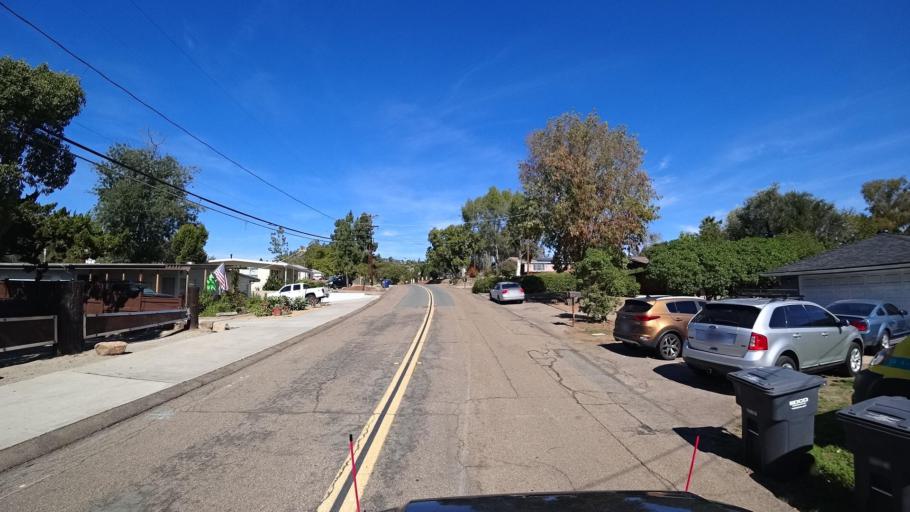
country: US
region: California
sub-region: San Diego County
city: Casa de Oro-Mount Helix
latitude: 32.7520
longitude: -116.9666
